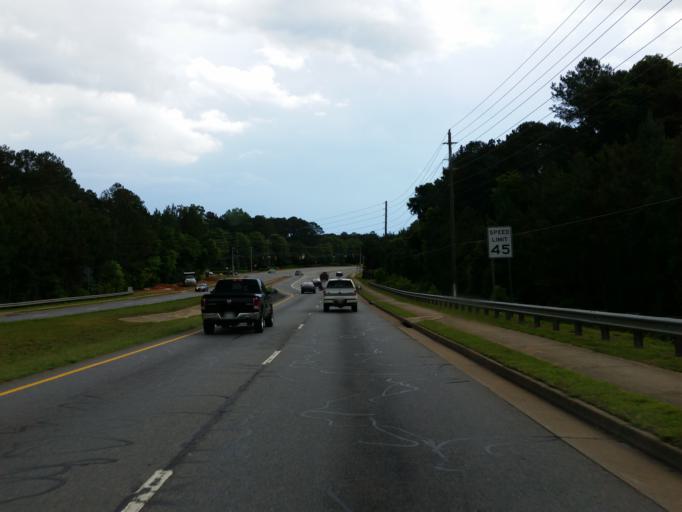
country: US
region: Georgia
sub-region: Cherokee County
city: Woodstock
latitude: 34.0874
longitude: -84.4930
